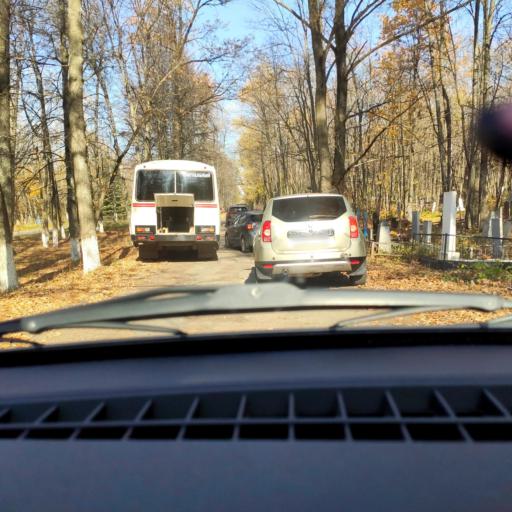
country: RU
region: Bashkortostan
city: Mikhaylovka
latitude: 54.8082
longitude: 55.8633
